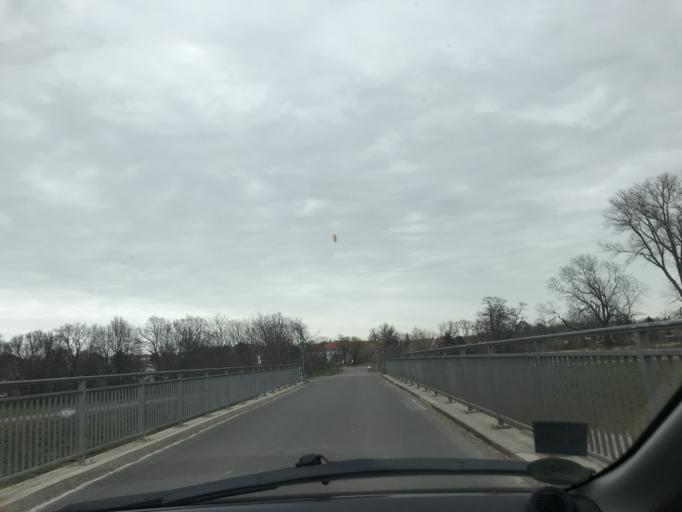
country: DE
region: Saxony
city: Schkeuditz
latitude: 51.3806
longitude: 12.2697
